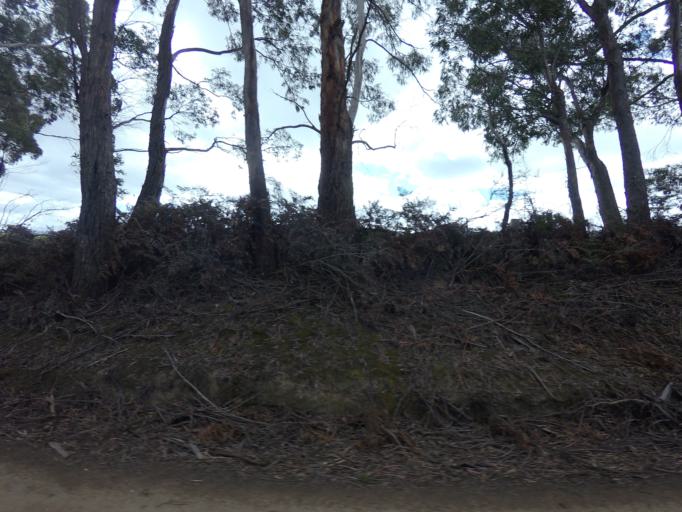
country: AU
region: Tasmania
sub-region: Huon Valley
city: Geeveston
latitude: -43.4260
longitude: 146.9978
